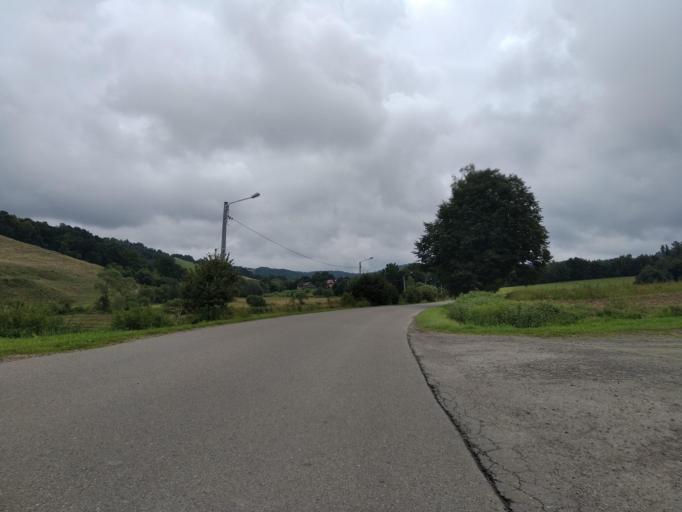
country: PL
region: Subcarpathian Voivodeship
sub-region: Powiat brzozowski
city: Nozdrzec
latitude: 49.7322
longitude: 22.2704
